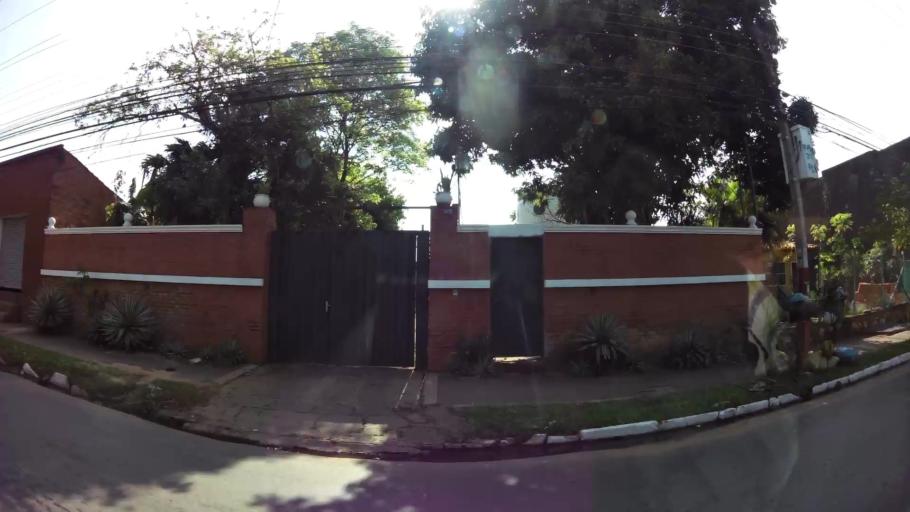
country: PY
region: Central
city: Fernando de la Mora
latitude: -25.3170
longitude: -57.5374
